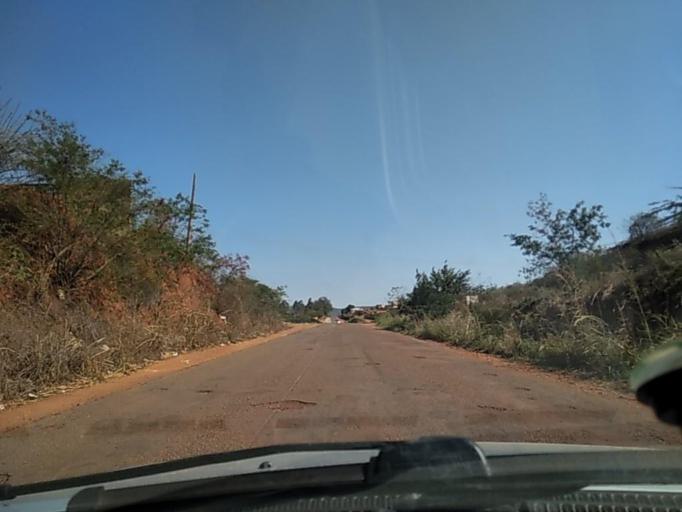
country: BR
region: Bahia
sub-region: Caetite
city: Caetite
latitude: -14.0472
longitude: -42.4853
